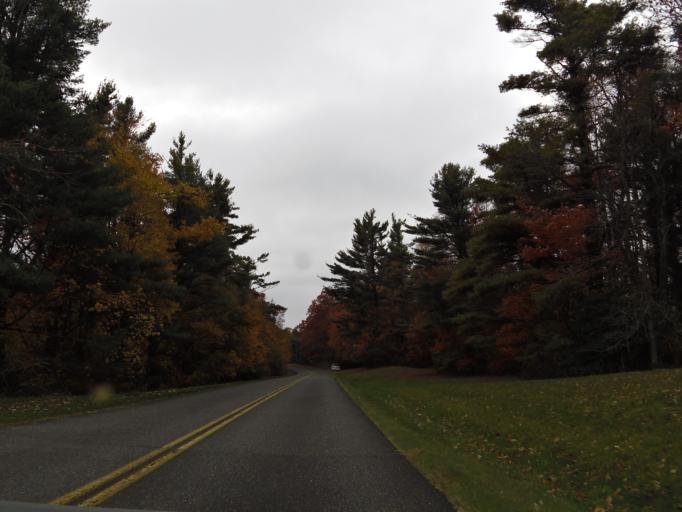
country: US
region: North Carolina
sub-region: Ashe County
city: West Jefferson
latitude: 36.2919
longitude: -81.4067
